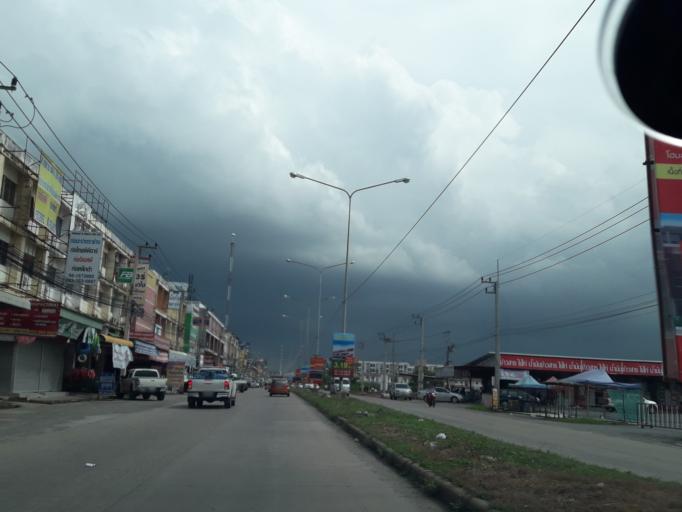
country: TH
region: Pathum Thani
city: Khlong Luang
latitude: 14.0737
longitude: 100.6340
